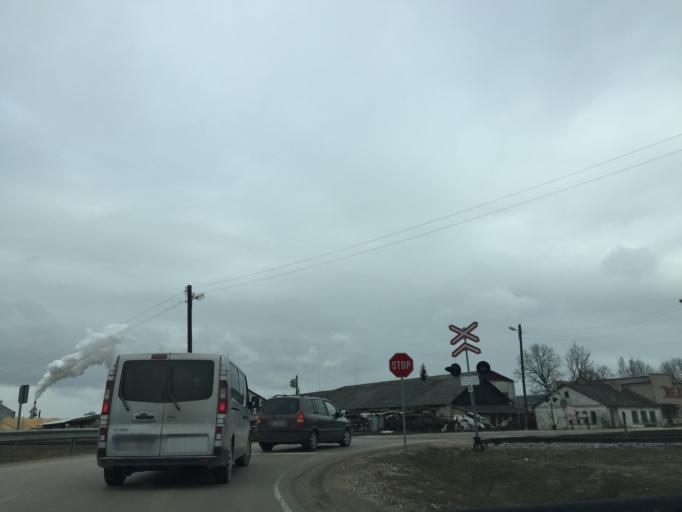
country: LV
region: Kraslavas Rajons
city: Kraslava
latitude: 55.9265
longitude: 27.1414
